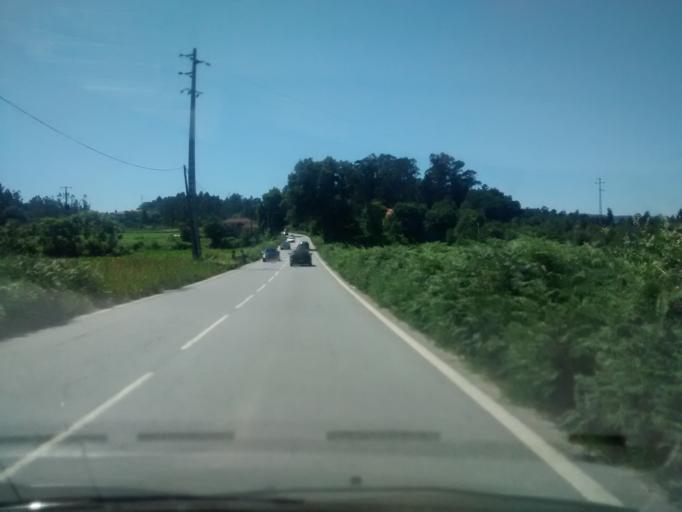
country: PT
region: Braga
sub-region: Barcelos
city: Galegos
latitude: 41.5314
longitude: -8.5454
